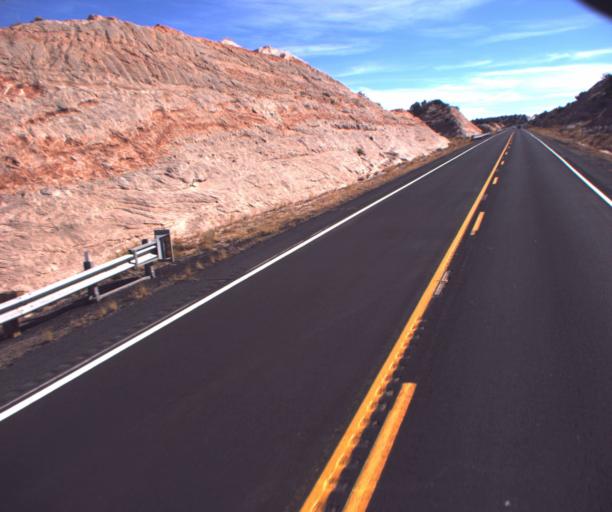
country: US
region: Arizona
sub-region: Coconino County
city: Kaibito
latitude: 36.5955
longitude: -110.9090
